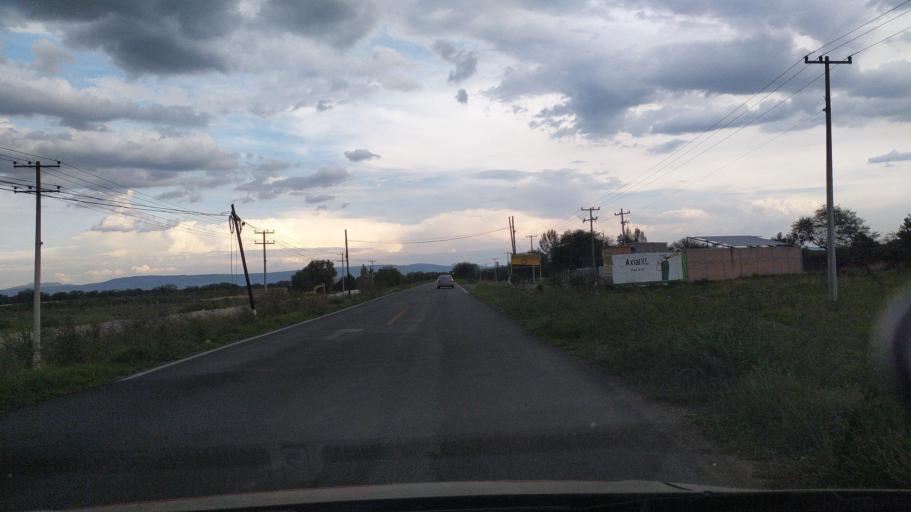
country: MX
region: Guanajuato
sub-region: San Francisco del Rincon
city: San Ignacio de Hidalgo
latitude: 20.8249
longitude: -101.9030
